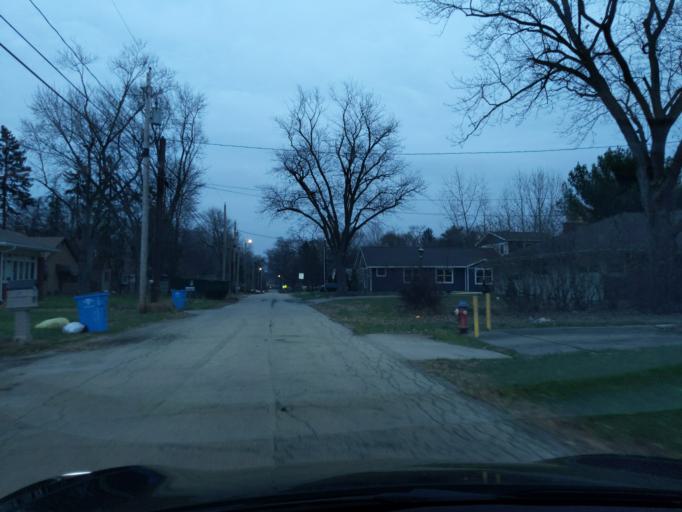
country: US
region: Indiana
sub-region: Saint Joseph County
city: Notre Dame
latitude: 41.7173
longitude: -86.2499
